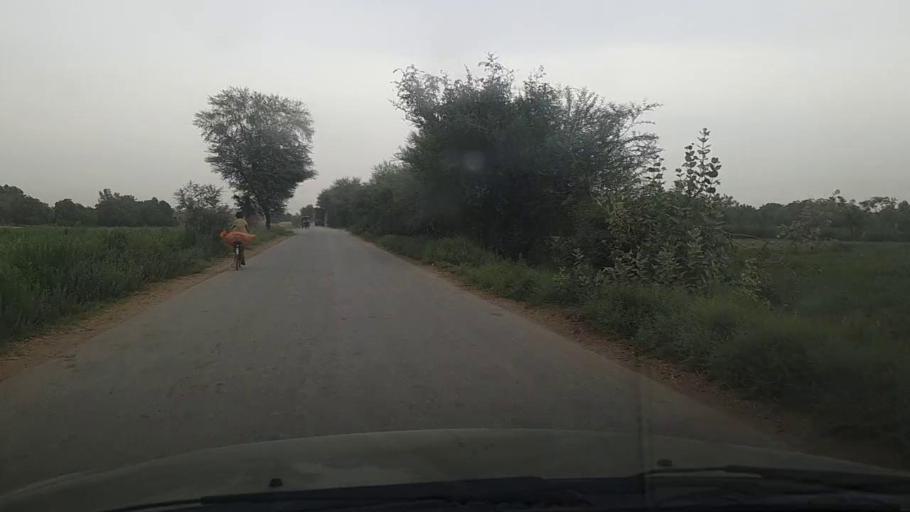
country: PK
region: Sindh
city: Daulatpur
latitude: 26.3189
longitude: 68.1039
